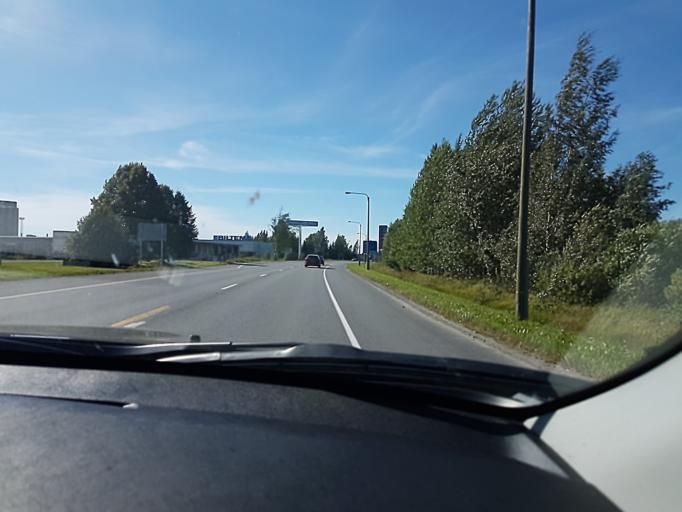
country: FI
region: Southern Ostrobothnia
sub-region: Seinaejoki
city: Nurmo
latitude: 62.7916
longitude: 22.8852
